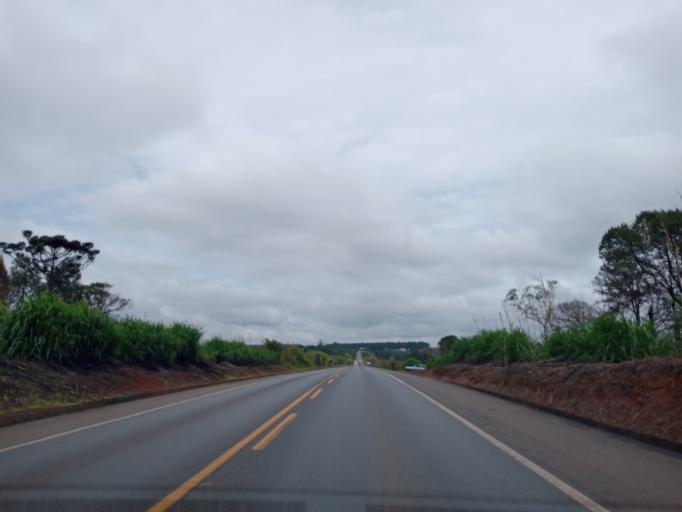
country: BR
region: Minas Gerais
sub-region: Campos Altos
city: Campos Altos
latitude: -19.6550
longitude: -46.1885
